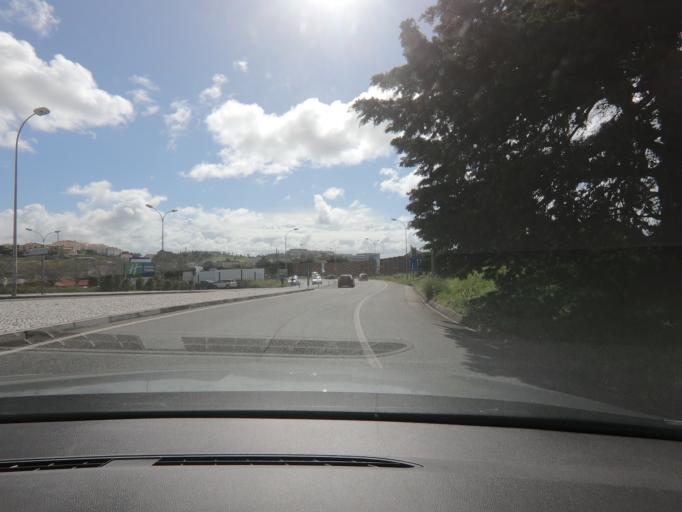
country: PT
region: Lisbon
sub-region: Oeiras
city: Porto Salvo
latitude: 38.7145
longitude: -9.3003
